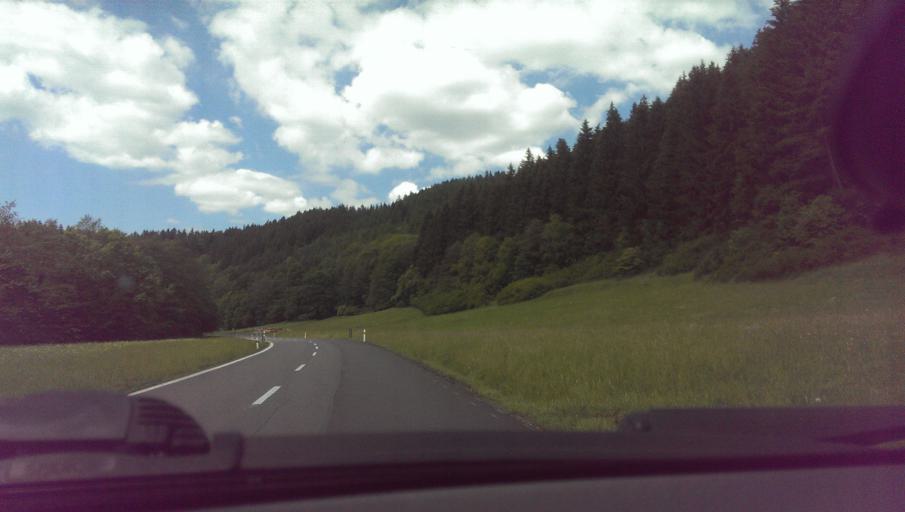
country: CZ
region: Zlin
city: Valasska Polanka
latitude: 49.2469
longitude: 17.9919
